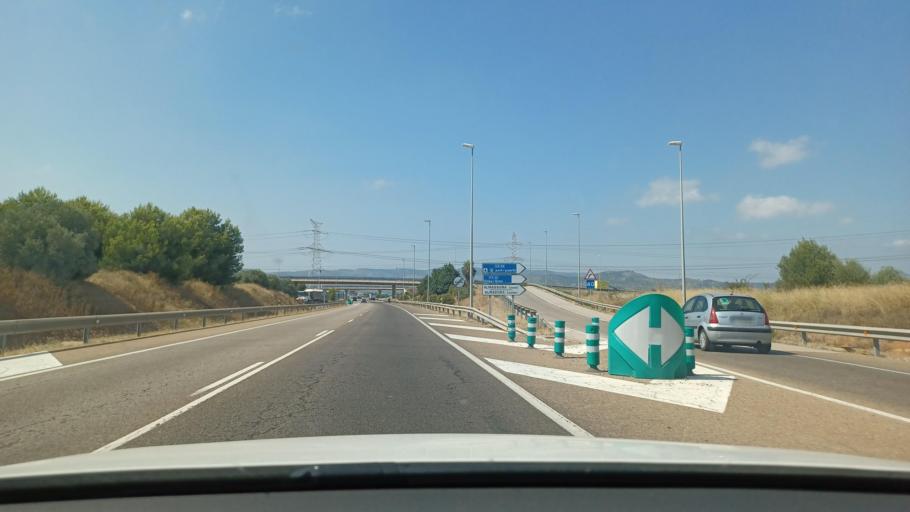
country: ES
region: Valencia
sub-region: Provincia de Castello
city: Vila-real
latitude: 39.9693
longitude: -0.0854
